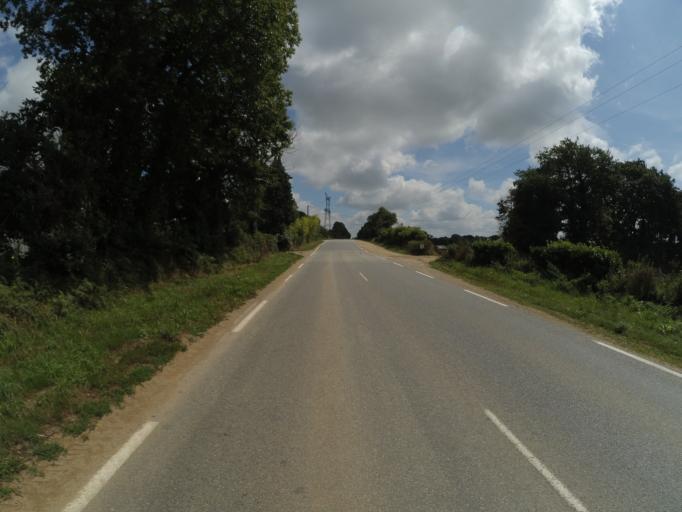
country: FR
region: Brittany
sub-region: Departement du Finistere
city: Elliant
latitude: 47.9680
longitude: -3.8774
